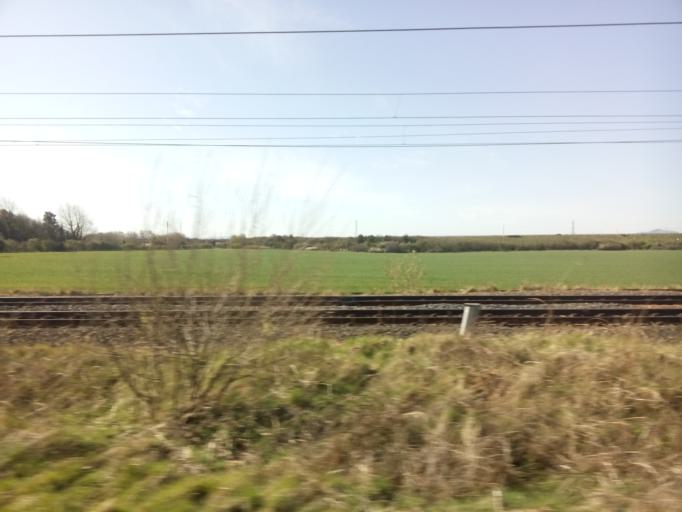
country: GB
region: Scotland
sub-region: East Lothian
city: Musselburgh
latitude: 55.9296
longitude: -3.0625
